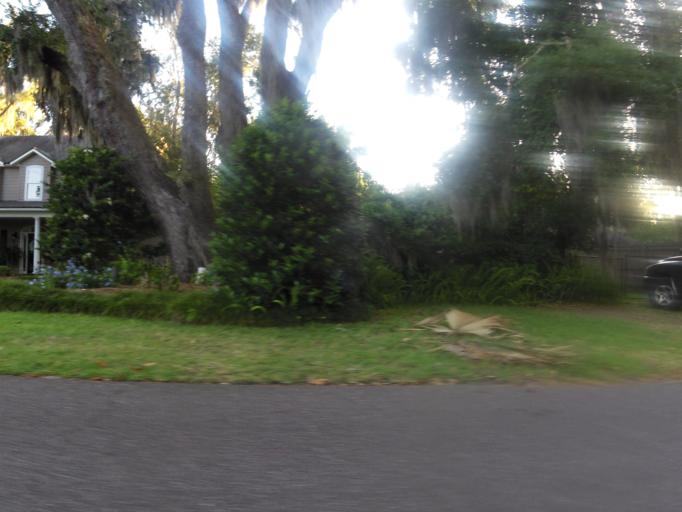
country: US
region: Florida
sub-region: Duval County
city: Jacksonville
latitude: 30.2684
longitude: -81.7074
